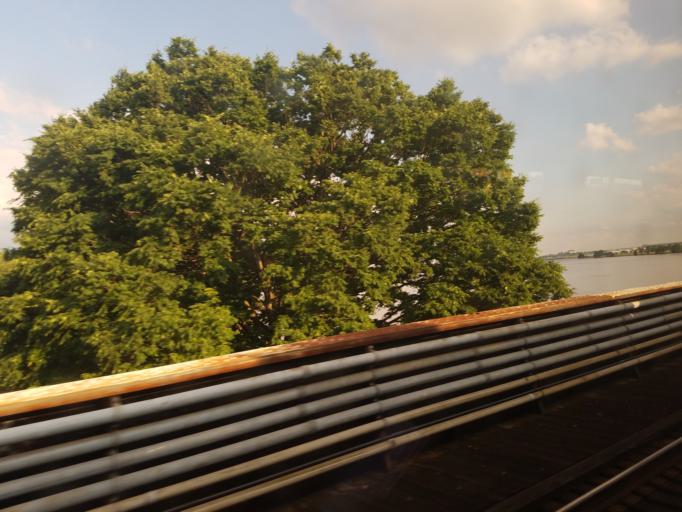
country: US
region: Washington, D.C.
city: Washington, D.C.
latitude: 38.8766
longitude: -77.0366
